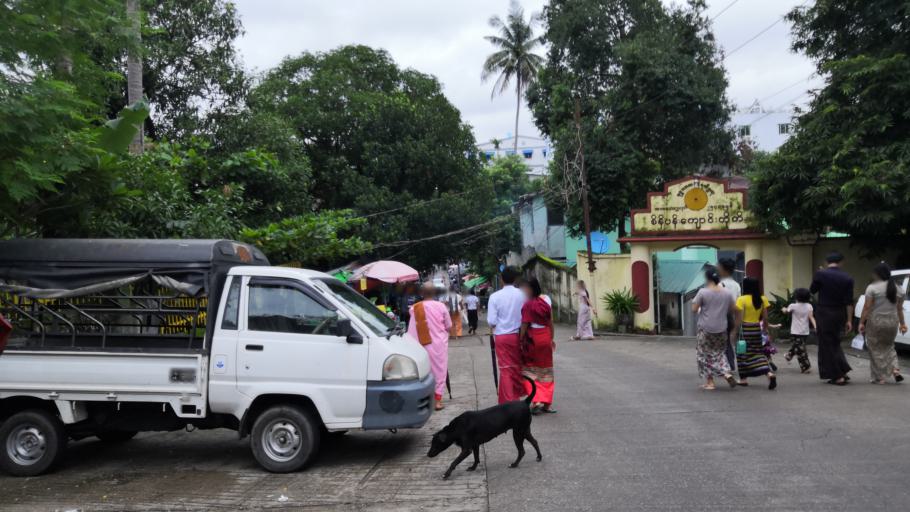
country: MM
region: Yangon
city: Yangon
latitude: 16.7979
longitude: 96.1524
